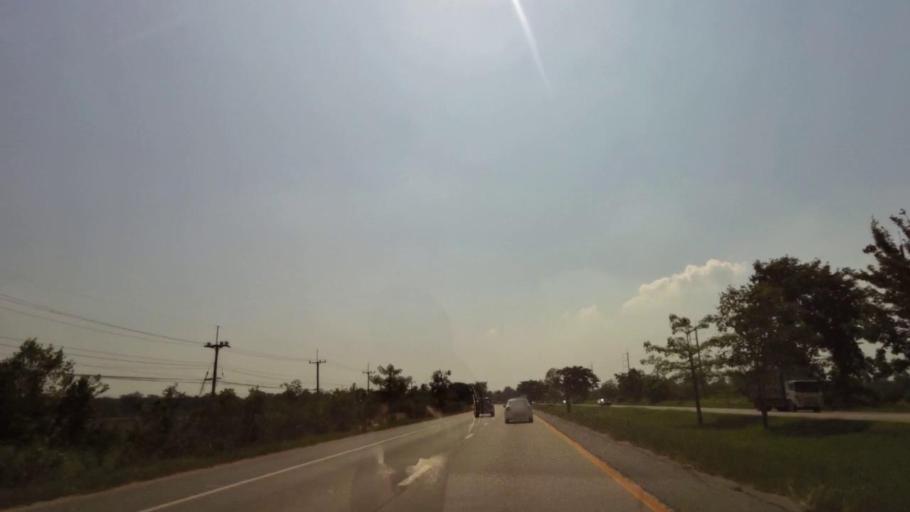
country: TH
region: Phichit
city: Wachira Barami
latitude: 16.5913
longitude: 100.1469
